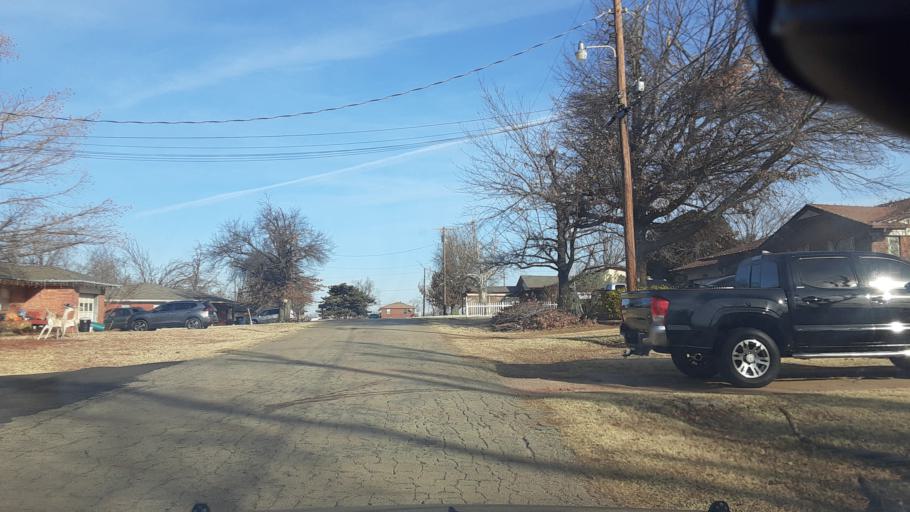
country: US
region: Oklahoma
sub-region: Logan County
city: Guthrie
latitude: 35.8549
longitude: -97.4309
